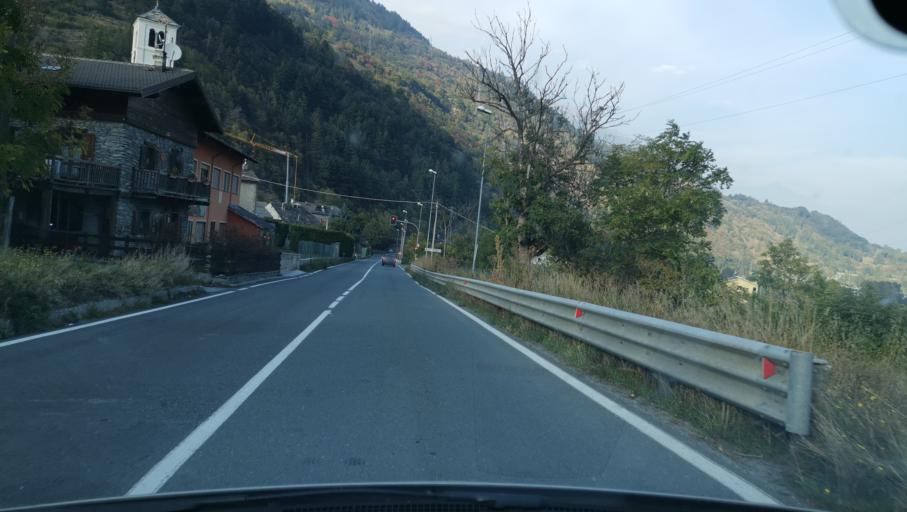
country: IT
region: Piedmont
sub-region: Provincia di Torino
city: Salbertrand
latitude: 45.0713
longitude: 6.8843
